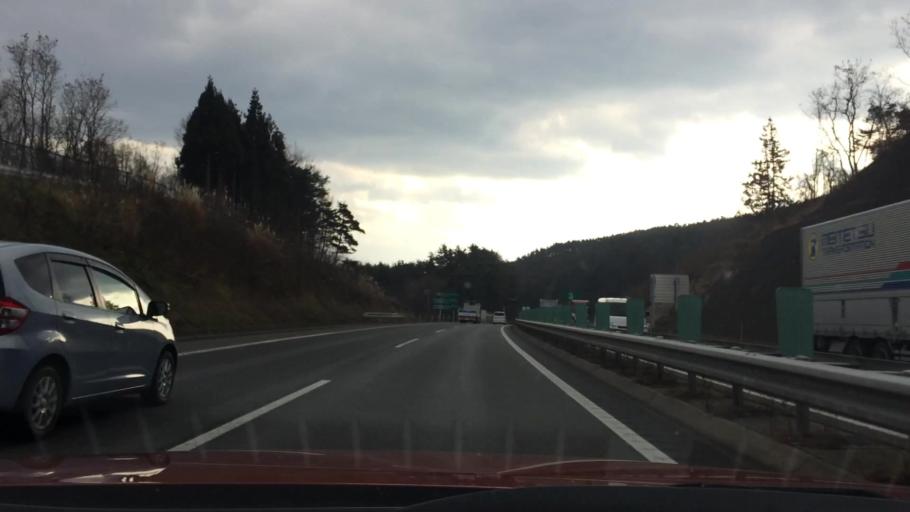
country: JP
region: Nagano
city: Okaya
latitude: 36.0769
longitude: 138.0389
